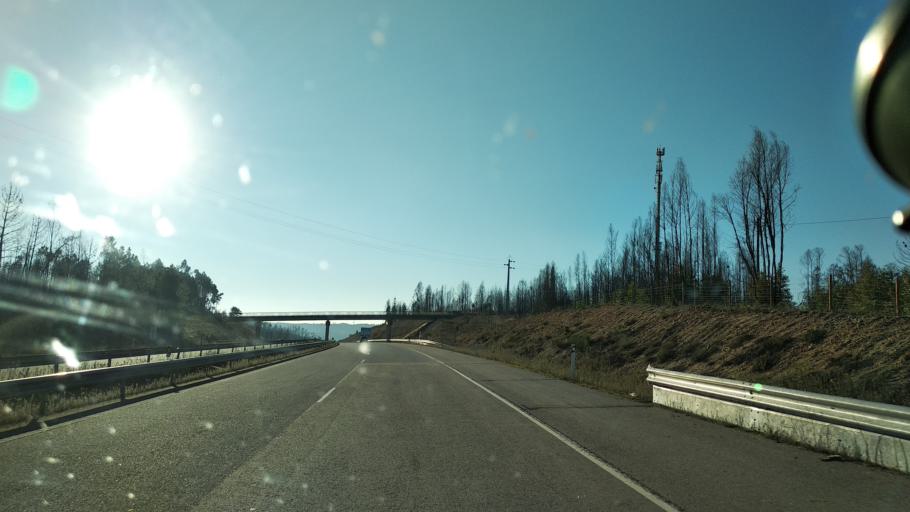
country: PT
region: Santarem
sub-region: Macao
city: Macao
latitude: 39.5289
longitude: -7.9553
